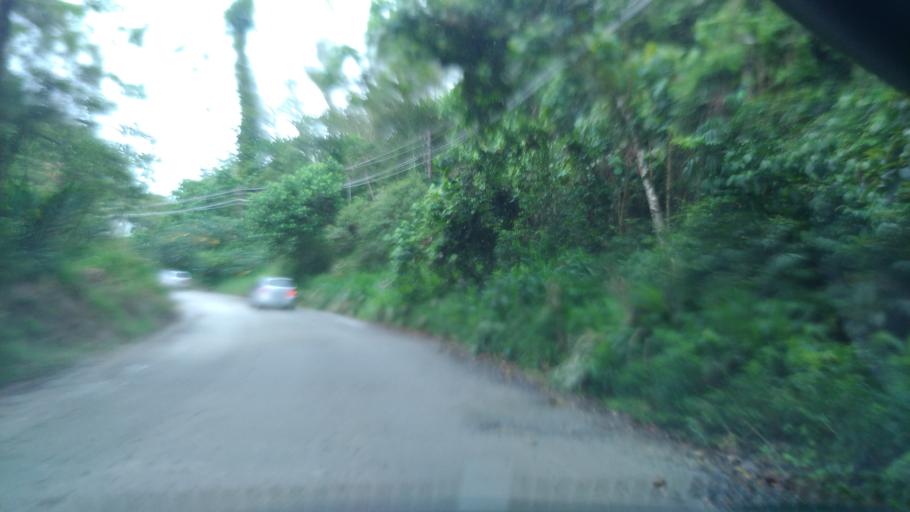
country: BR
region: Sao Paulo
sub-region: Sao Bernardo Do Campo
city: Sao Bernardo do Campo
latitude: -23.7427
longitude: -46.5131
